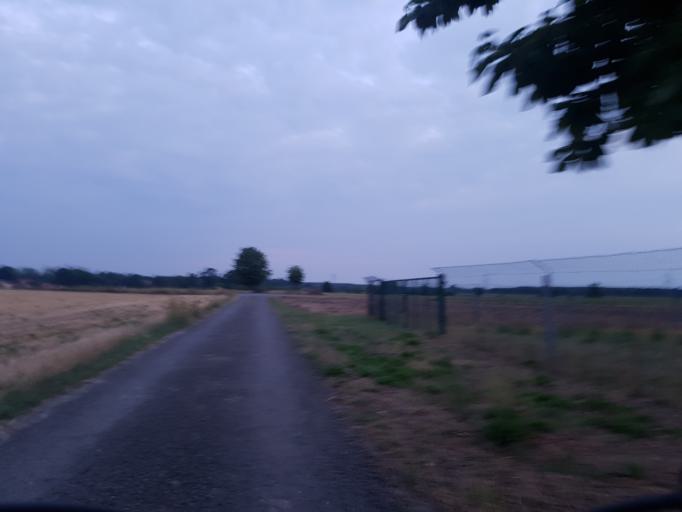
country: DE
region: Brandenburg
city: Bad Liebenwerda
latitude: 51.5514
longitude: 13.4181
